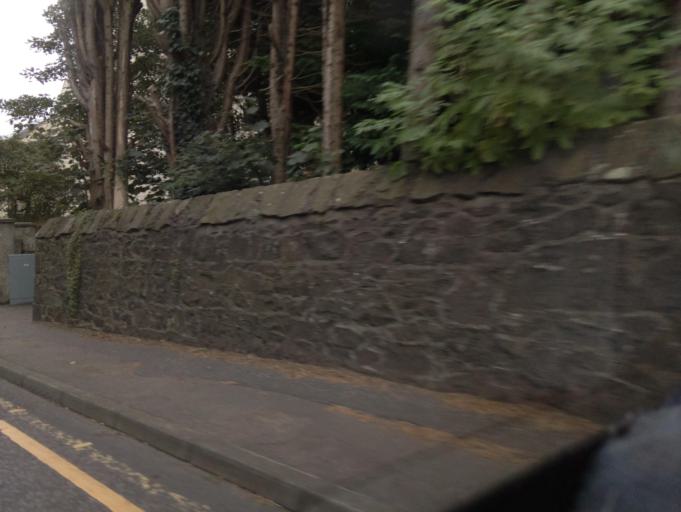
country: GB
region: Scotland
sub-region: Fife
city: Leslie
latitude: 56.2012
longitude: -3.2169
